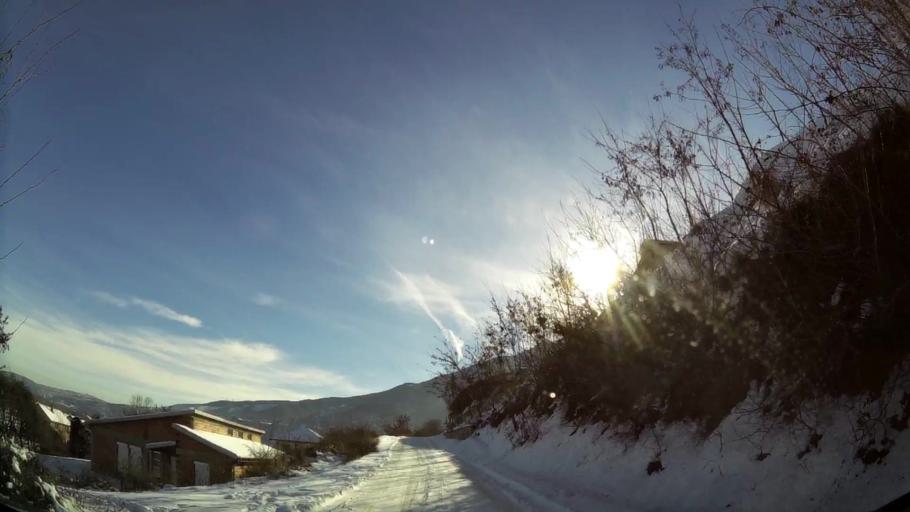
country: MK
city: Ljubin
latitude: 41.9811
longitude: 21.3011
